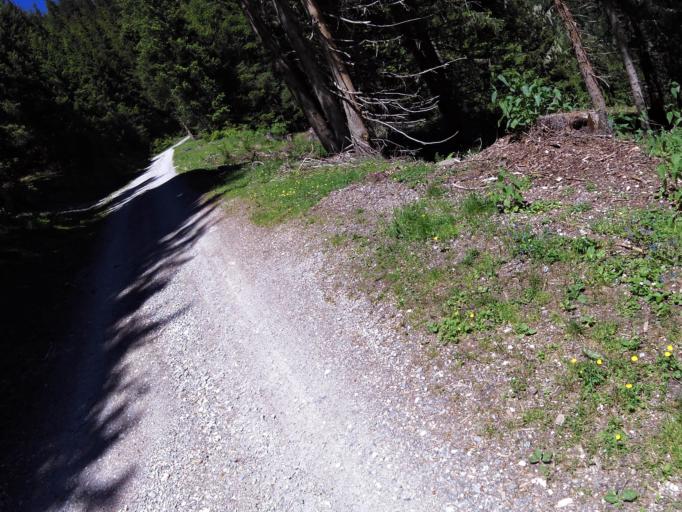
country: AT
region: Tyrol
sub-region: Politischer Bezirk Innsbruck Land
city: Neustift im Stubaital
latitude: 47.1162
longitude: 11.2887
